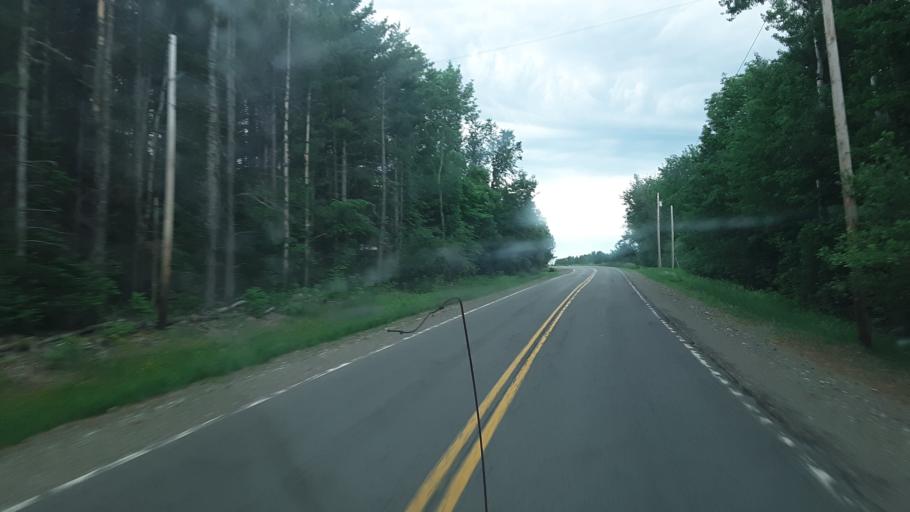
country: US
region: Maine
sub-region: Penobscot County
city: Patten
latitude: 45.7664
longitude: -68.3121
